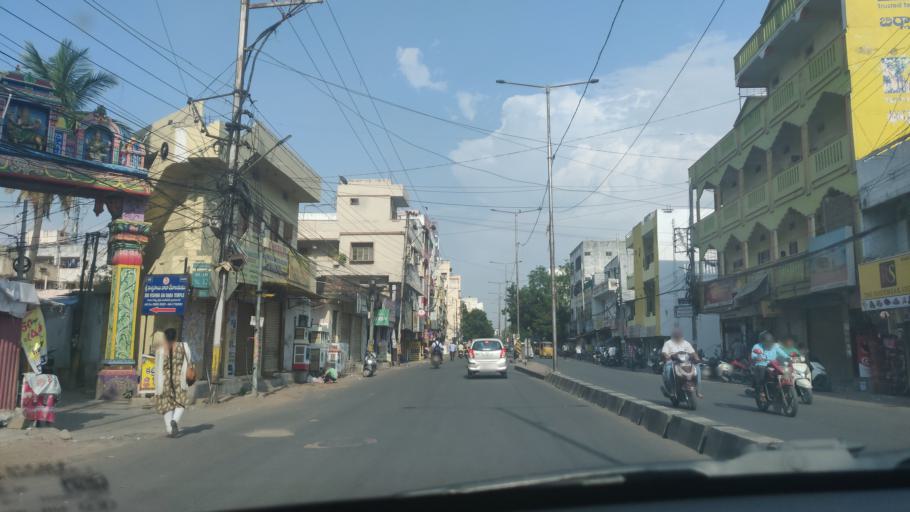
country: IN
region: Telangana
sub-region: Rangareddi
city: Gaddi Annaram
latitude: 17.3942
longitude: 78.5084
